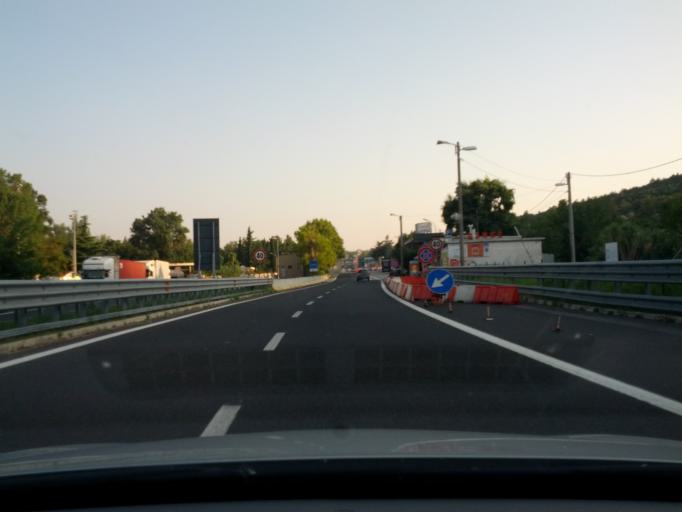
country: SI
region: Koper-Capodistria
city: Spodnje Skofije
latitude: 45.5843
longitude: 13.7978
